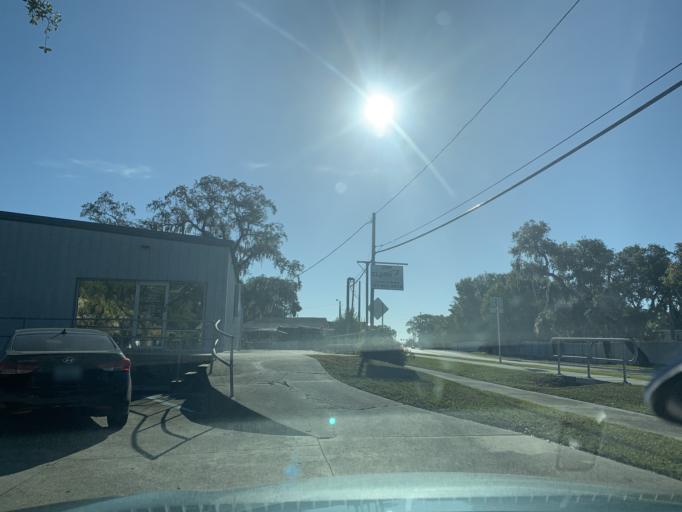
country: US
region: Florida
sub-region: Pinellas County
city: Lealman
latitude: 27.8267
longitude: -82.6739
